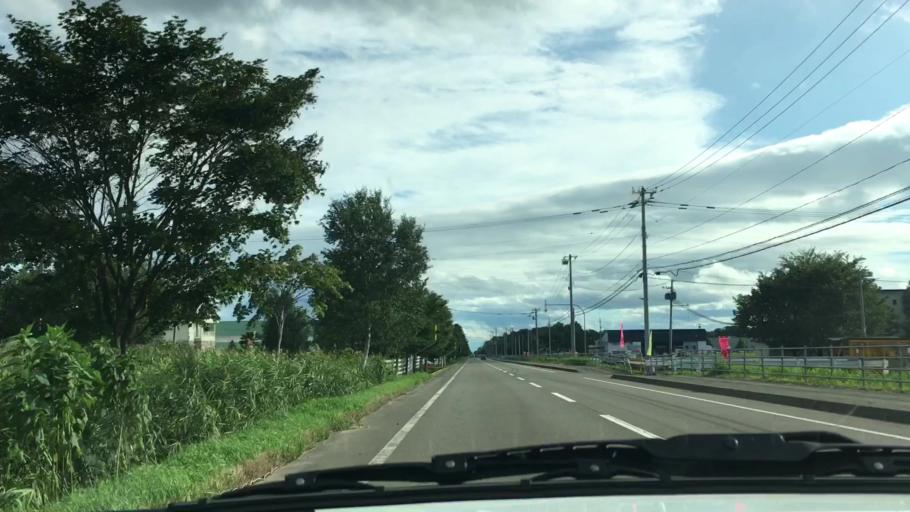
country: JP
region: Hokkaido
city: Otofuke
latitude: 43.2533
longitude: 143.2997
